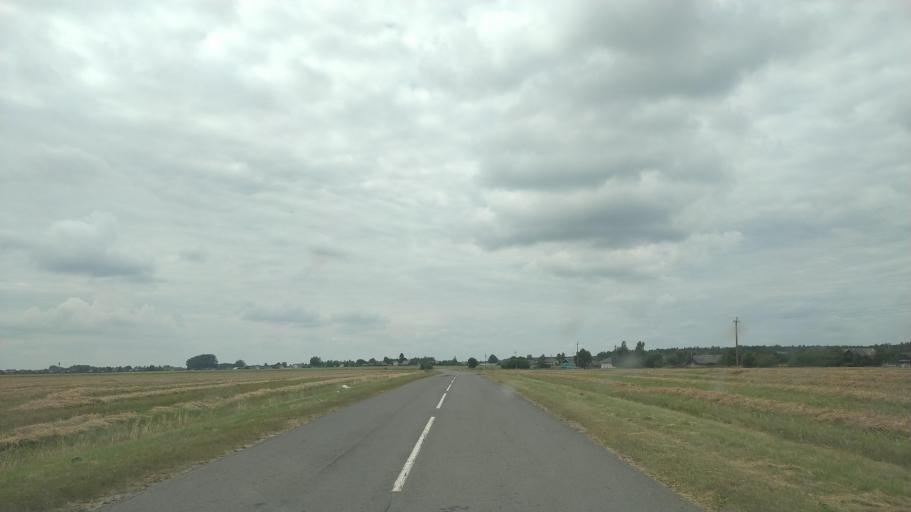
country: BY
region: Brest
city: Byelaazyorsk
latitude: 52.5403
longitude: 25.1179
